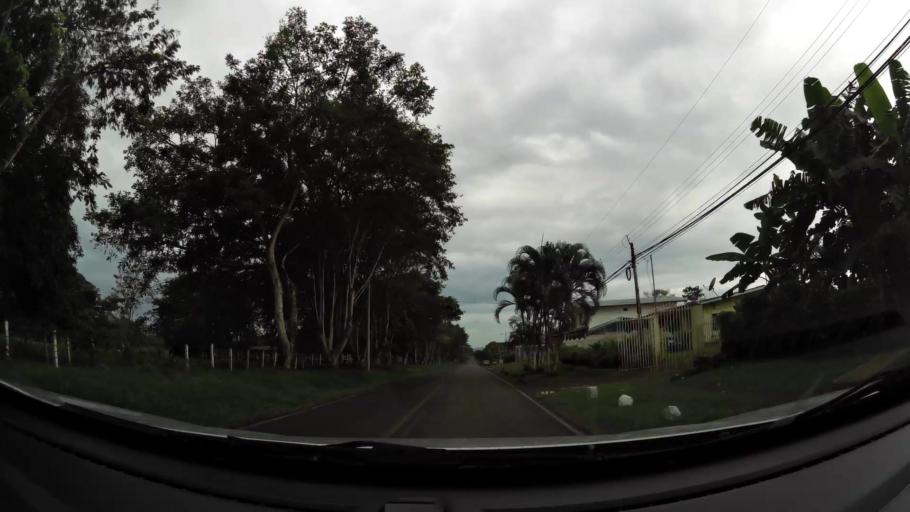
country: CR
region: Puntarenas
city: Esparza
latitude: 9.9747
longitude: -84.6185
